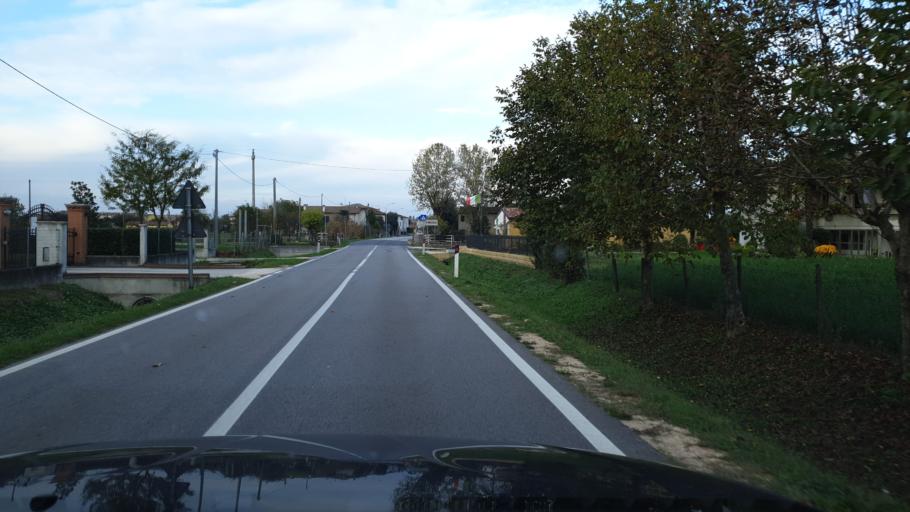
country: IT
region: Veneto
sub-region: Provincia di Padova
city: Conselve
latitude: 45.2274
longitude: 11.8630
